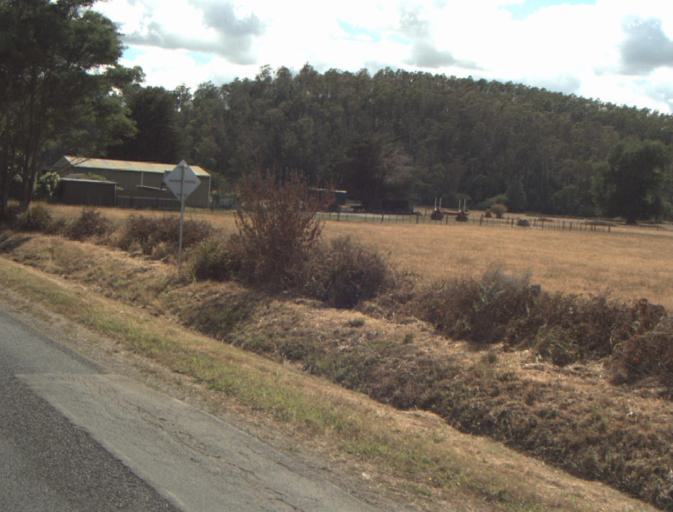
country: AU
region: Tasmania
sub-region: Launceston
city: Mayfield
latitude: -41.2516
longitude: 147.1475
